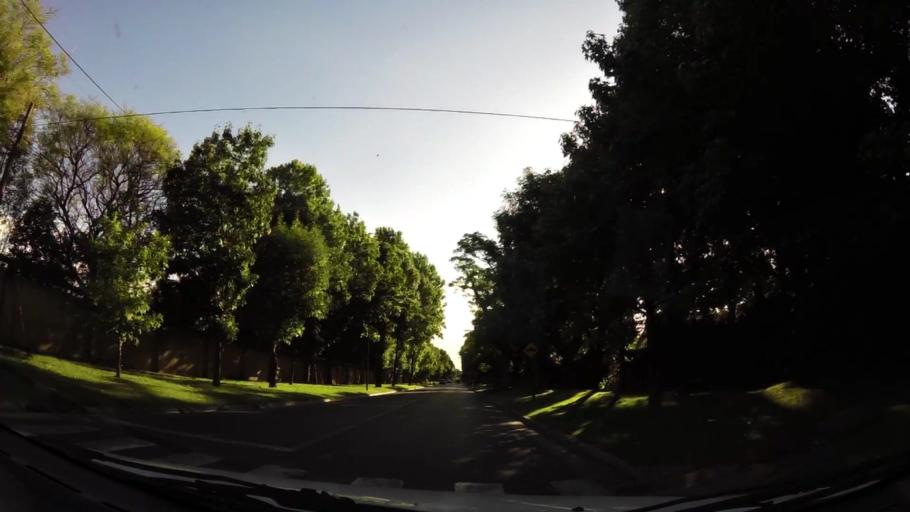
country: AR
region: Buenos Aires
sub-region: Partido de San Isidro
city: San Isidro
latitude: -34.4826
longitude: -58.5397
